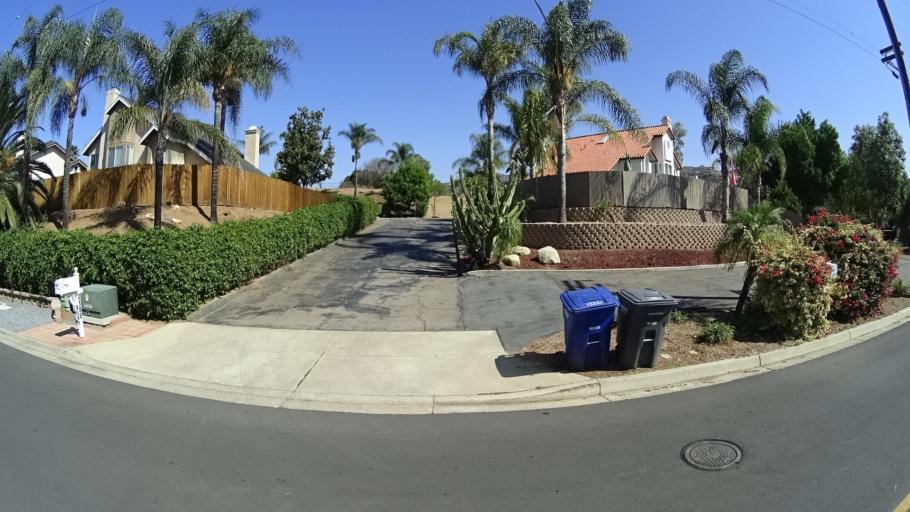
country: US
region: California
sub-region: San Diego County
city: Granite Hills
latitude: 32.7940
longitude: -116.9034
